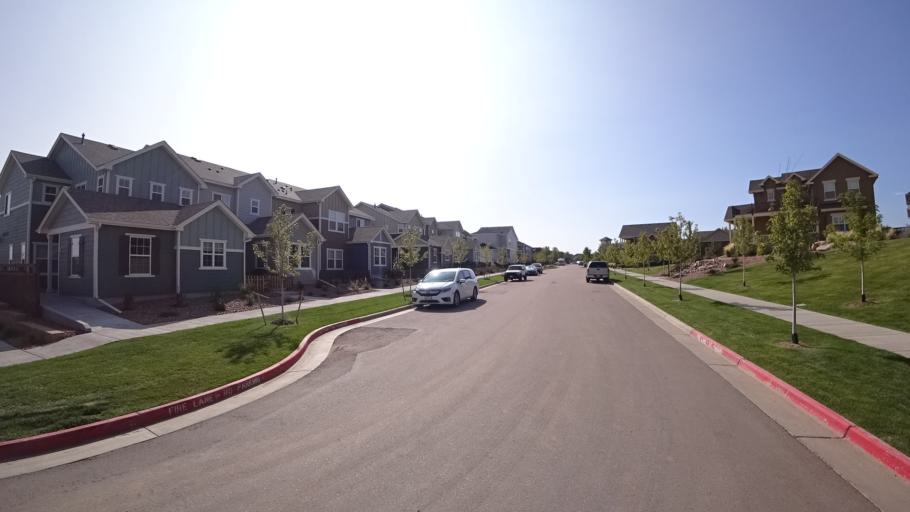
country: US
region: Colorado
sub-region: El Paso County
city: Colorado Springs
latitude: 38.8325
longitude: -104.8538
